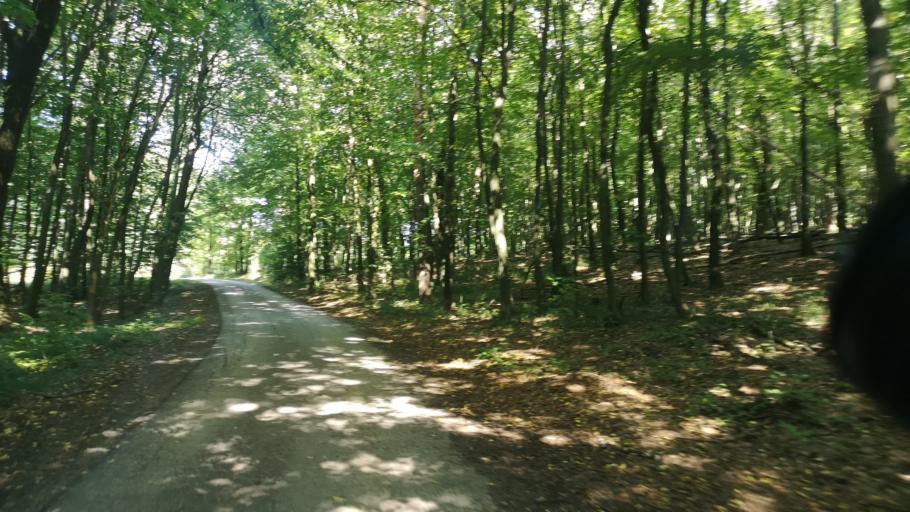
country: SK
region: Trnavsky
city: Smolenice
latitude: 48.5747
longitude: 17.4317
